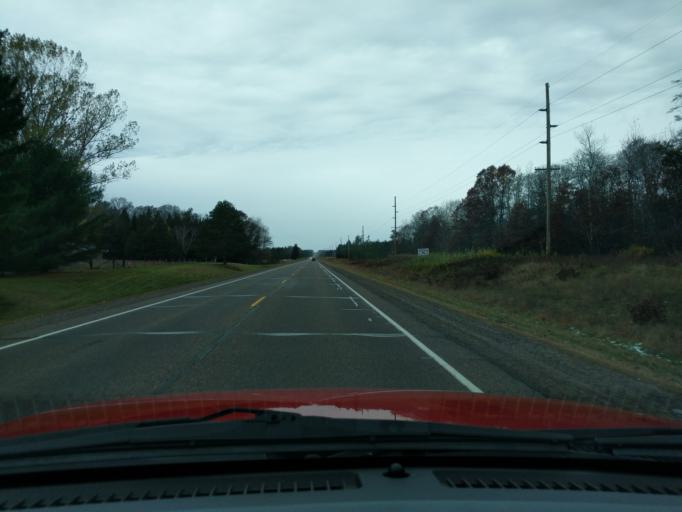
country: US
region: Wisconsin
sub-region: Washburn County
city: Spooner
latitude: 45.8151
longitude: -91.9785
